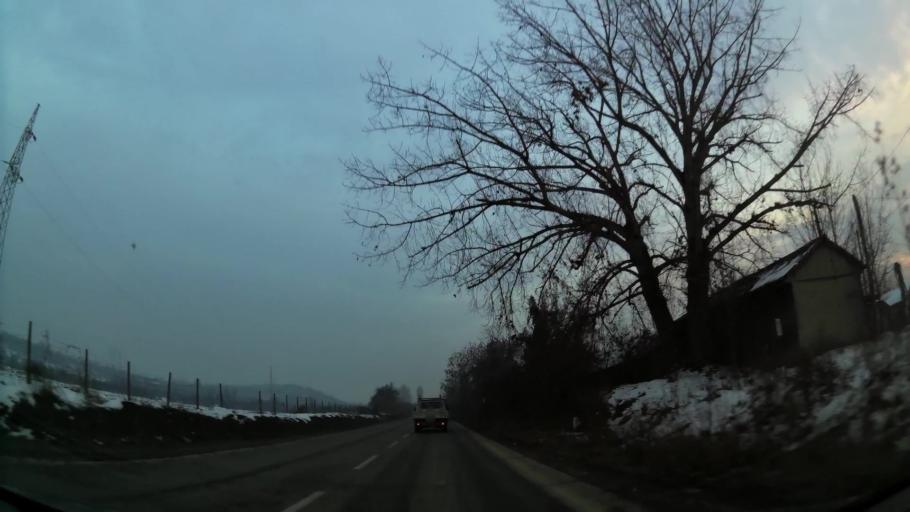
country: MK
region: Suto Orizari
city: Suto Orizare
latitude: 42.0216
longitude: 21.4097
